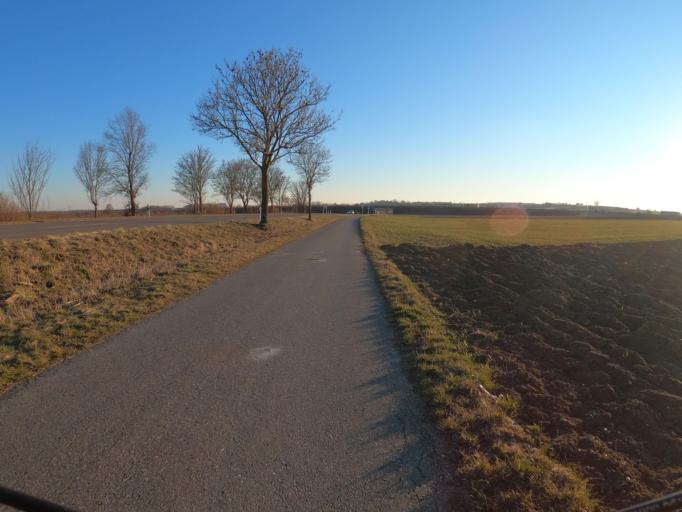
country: DE
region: Baden-Wuerttemberg
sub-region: Tuebingen Region
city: Langenau
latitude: 48.4772
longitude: 10.1134
